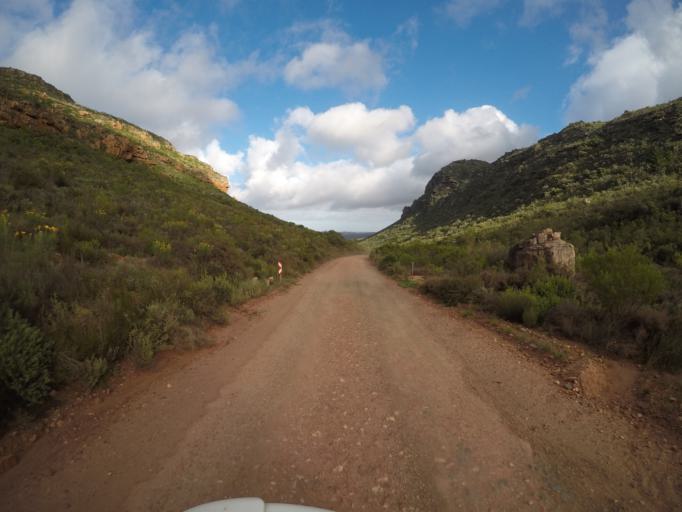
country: ZA
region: Western Cape
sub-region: West Coast District Municipality
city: Clanwilliam
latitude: -32.3412
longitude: 18.7906
